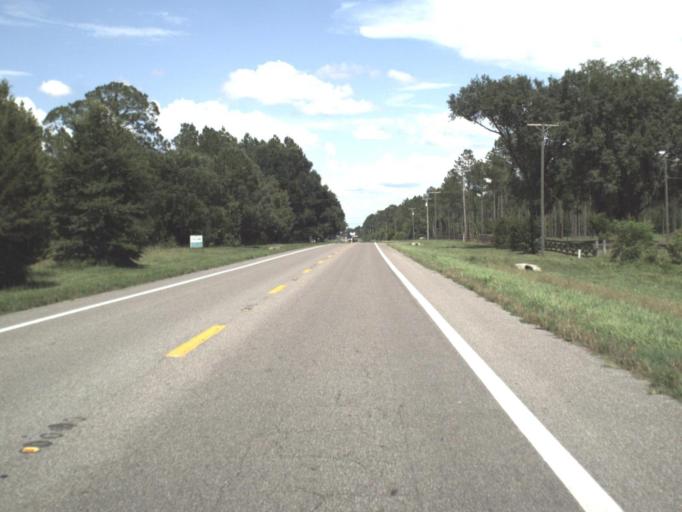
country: US
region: Florida
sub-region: Lafayette County
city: Mayo
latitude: 30.0530
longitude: -83.1471
